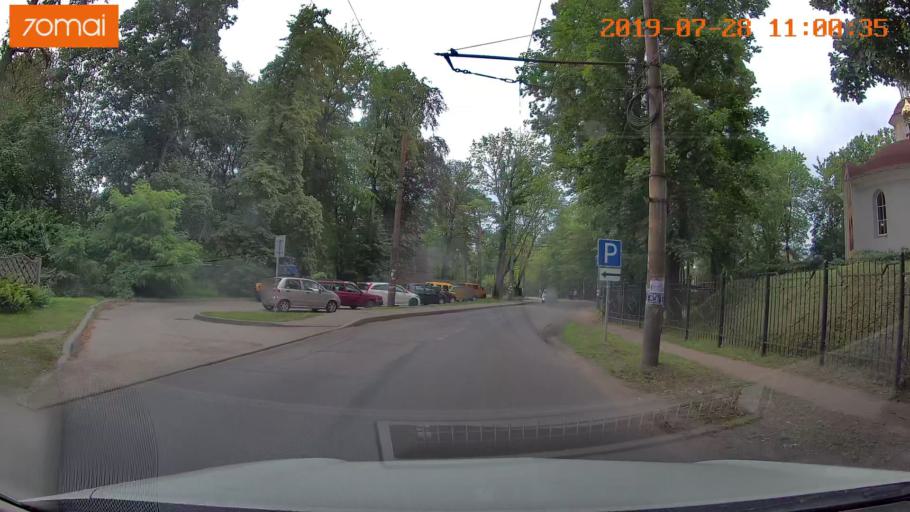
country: RU
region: Kaliningrad
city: Vzmorye
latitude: 54.7264
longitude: 20.3626
